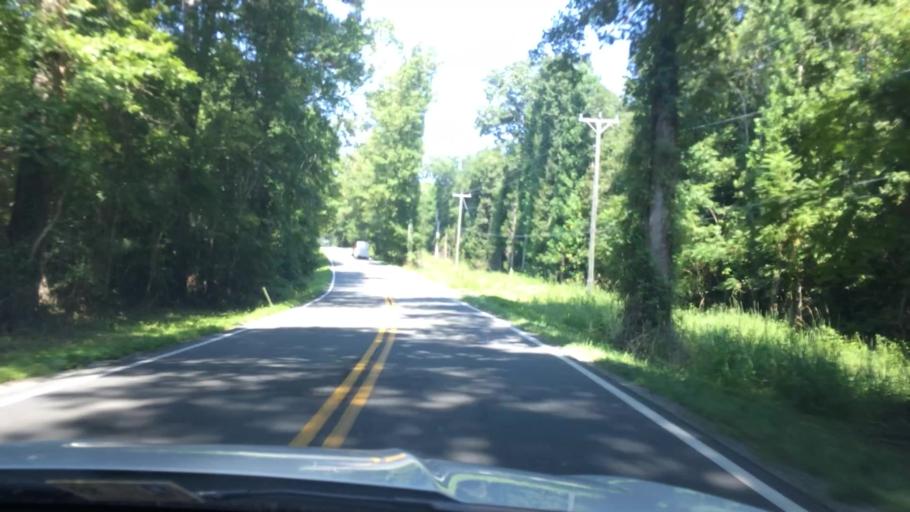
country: US
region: Virginia
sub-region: New Kent County
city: New Kent
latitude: 37.5186
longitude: -76.9973
